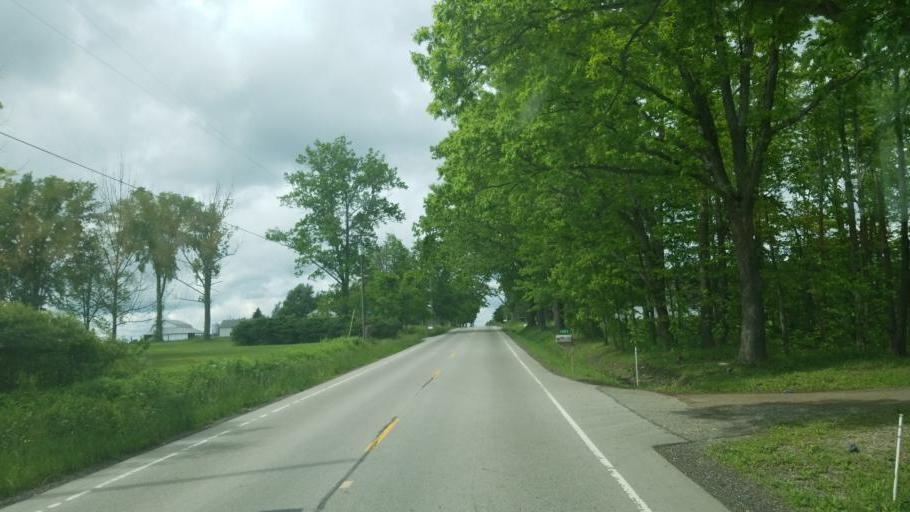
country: US
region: Ohio
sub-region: Portage County
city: Hiram
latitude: 41.3789
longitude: -81.1082
